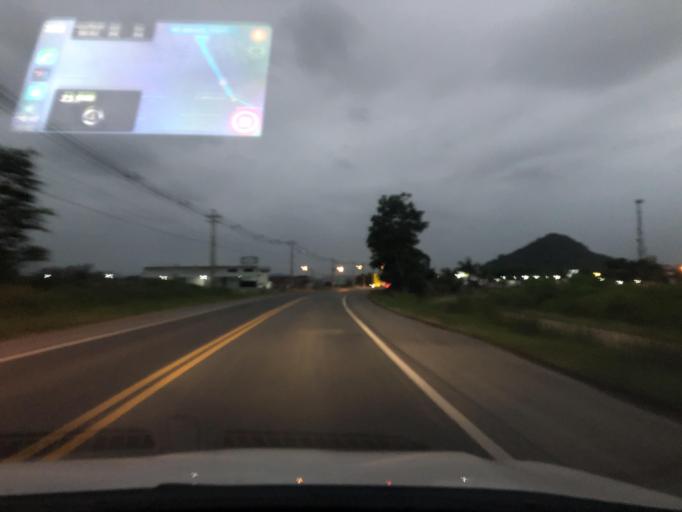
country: BR
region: Santa Catarina
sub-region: Jaragua Do Sul
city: Jaragua do Sul
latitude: -26.6146
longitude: -49.0126
